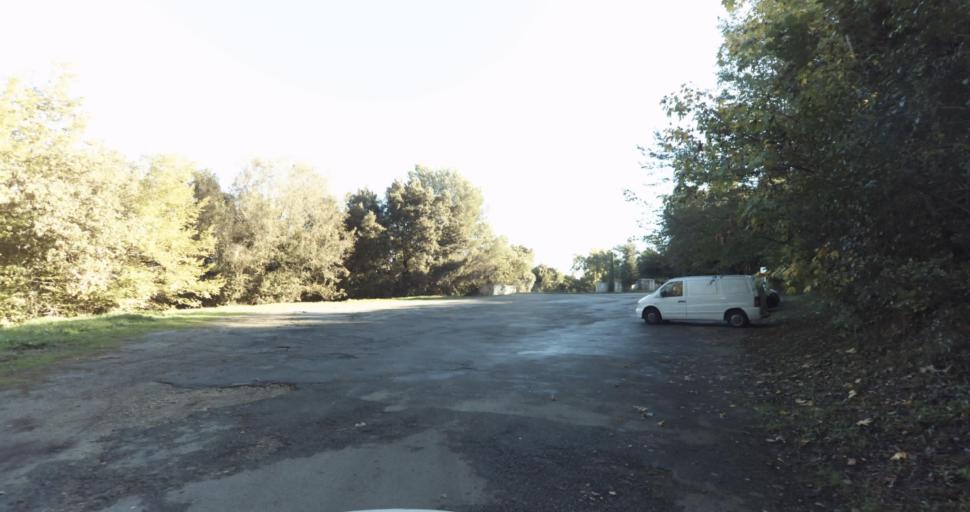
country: FR
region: Provence-Alpes-Cote d'Azur
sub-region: Departement des Alpes-Maritimes
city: La Colle-sur-Loup
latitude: 43.7074
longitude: 7.0965
